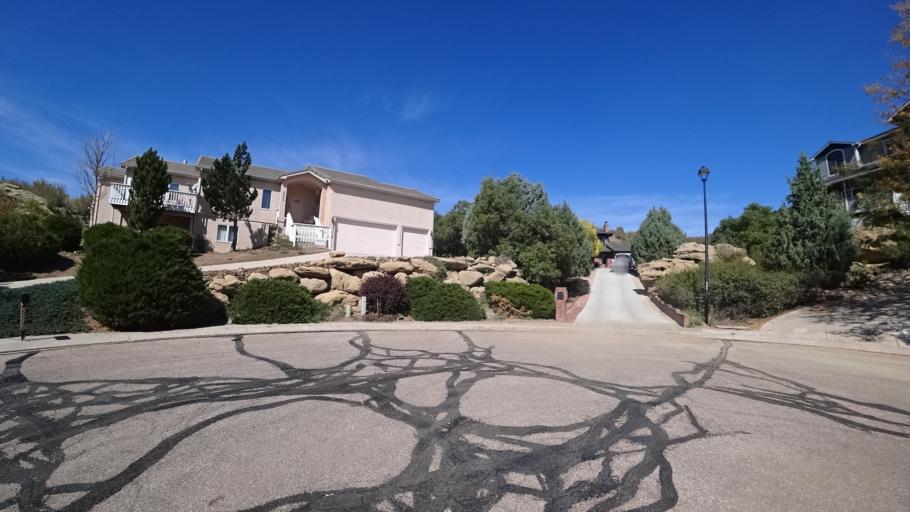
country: US
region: Colorado
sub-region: El Paso County
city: Cimarron Hills
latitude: 38.9135
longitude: -104.7509
